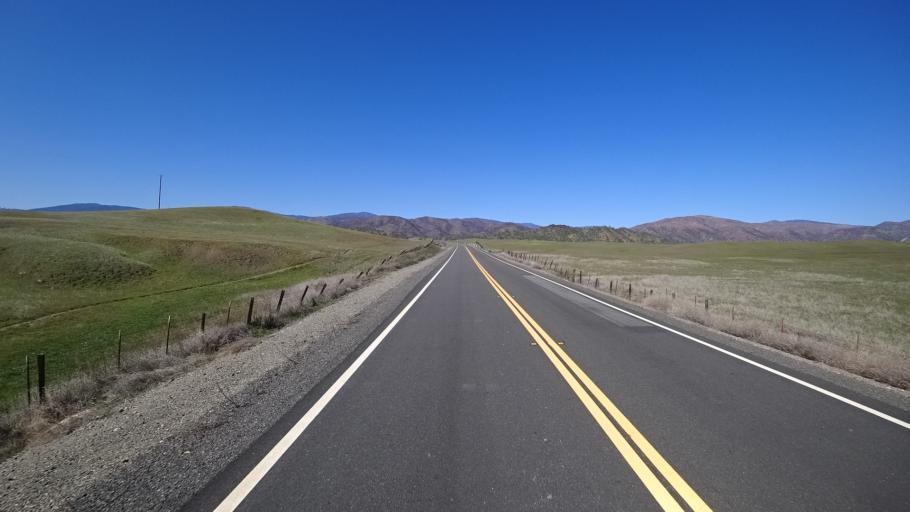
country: US
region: California
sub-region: Glenn County
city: Orland
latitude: 39.6594
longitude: -122.5471
